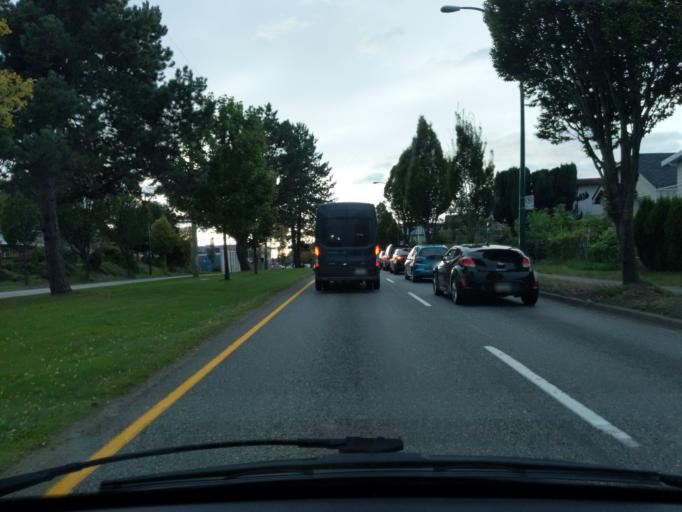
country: CA
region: British Columbia
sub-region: Fraser Valley Regional District
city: North Vancouver
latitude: 49.2695
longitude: -123.0422
